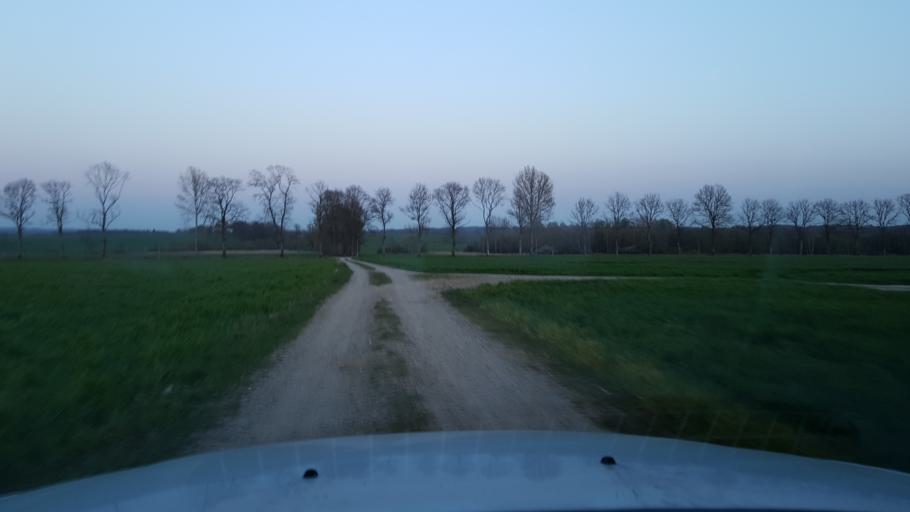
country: PL
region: West Pomeranian Voivodeship
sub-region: Powiat bialogardzki
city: Bialogard
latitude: 53.9593
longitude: 15.9667
